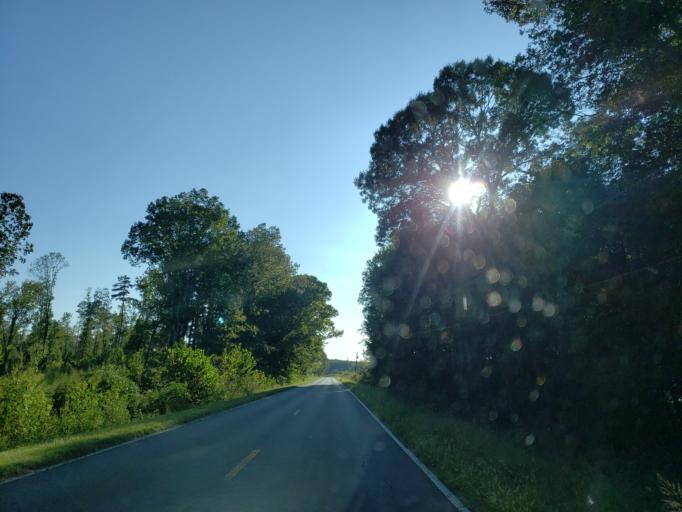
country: US
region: Georgia
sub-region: Bartow County
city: Rydal
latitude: 34.2936
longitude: -84.7861
